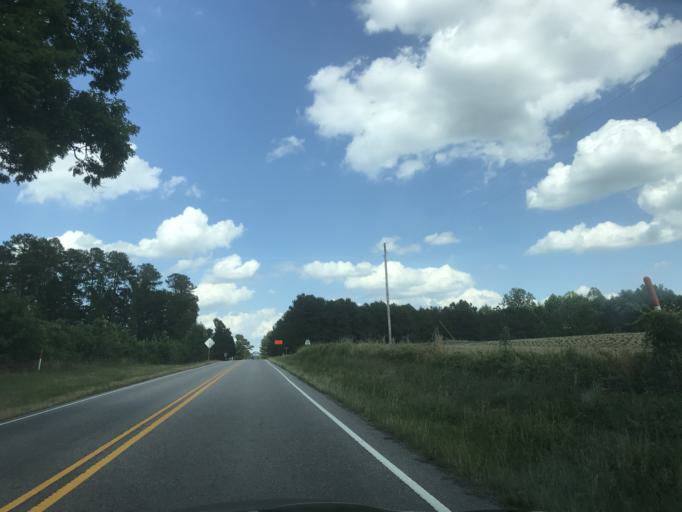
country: US
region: North Carolina
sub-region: Wake County
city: Rolesville
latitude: 35.9697
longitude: -78.3945
